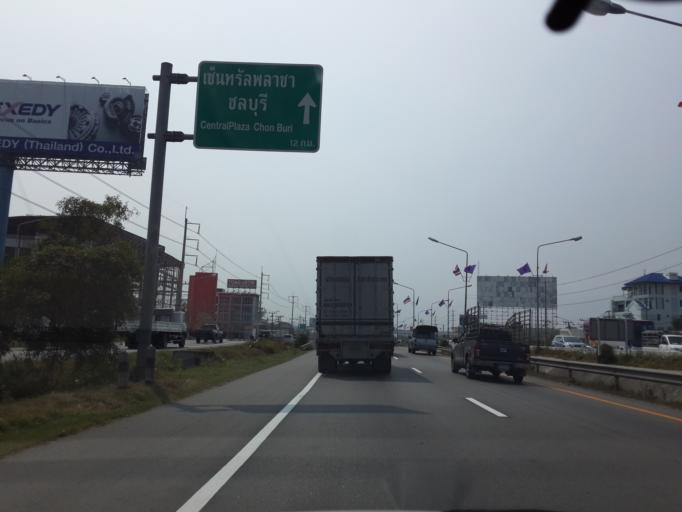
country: TH
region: Chon Buri
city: Chon Buri
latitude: 13.4451
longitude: 100.9997
